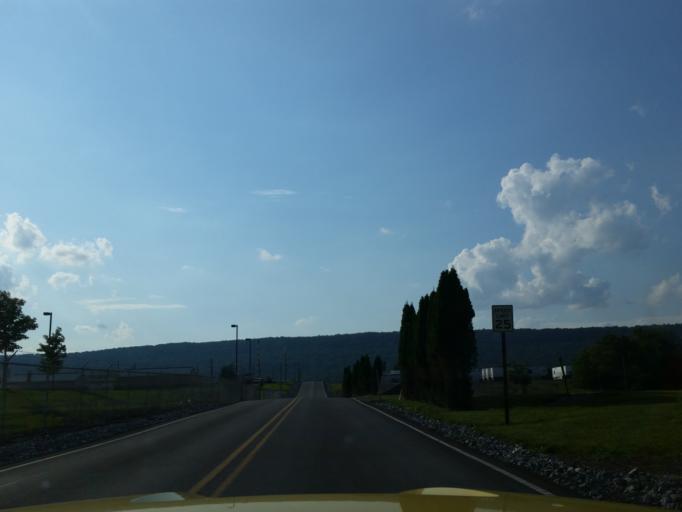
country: US
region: Pennsylvania
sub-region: Lebanon County
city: Jonestown
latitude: 40.4314
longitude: -76.5595
